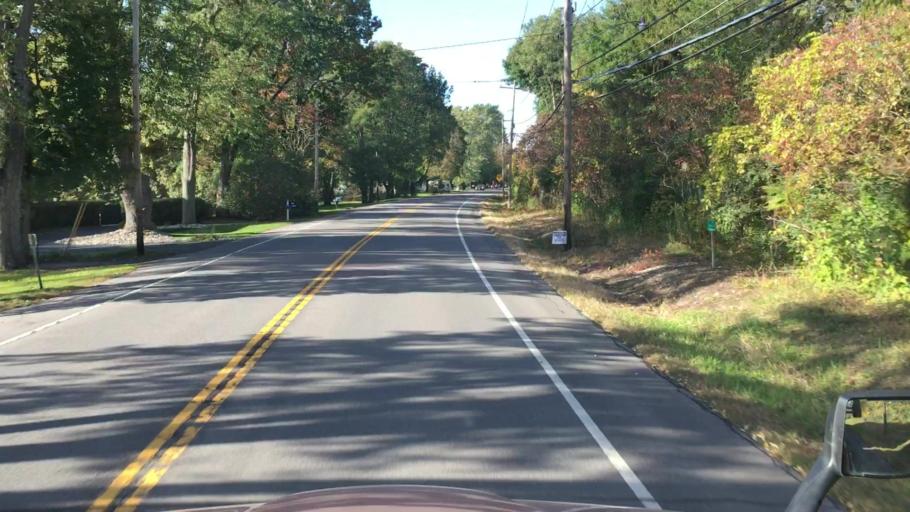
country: US
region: New York
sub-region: Schenectady County
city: Scotia
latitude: 42.8422
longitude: -73.9956
